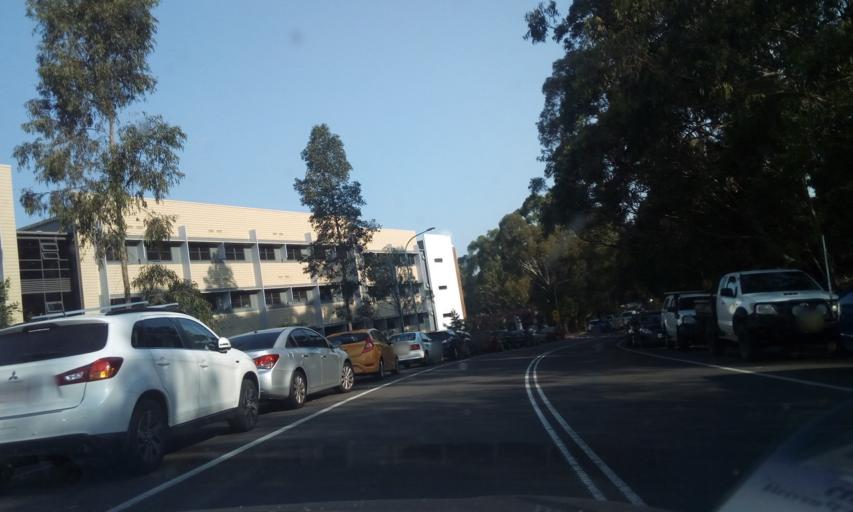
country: AU
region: New South Wales
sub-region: Wollongong
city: Mount Ousley
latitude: -34.4054
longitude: 150.8730
